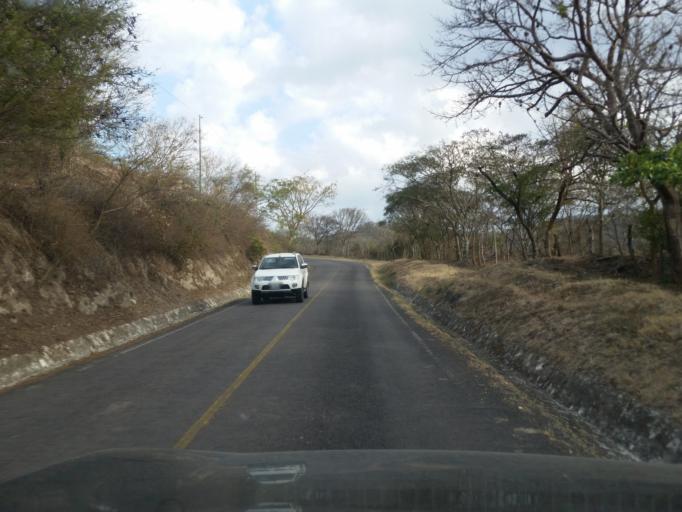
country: NI
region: Jinotega
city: San Rafael del Norte
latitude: 13.1957
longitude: -86.1334
